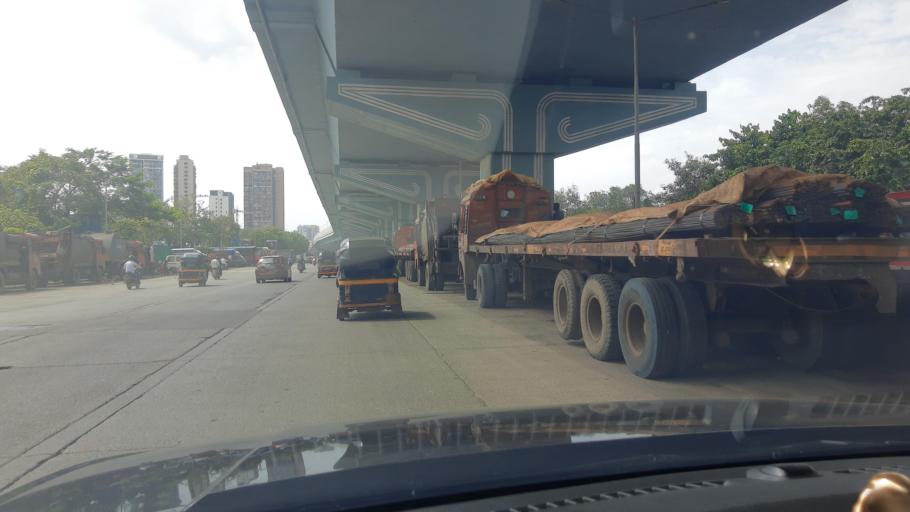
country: IN
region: Maharashtra
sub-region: Mumbai Suburban
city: Mumbai
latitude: 19.0598
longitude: 72.9229
